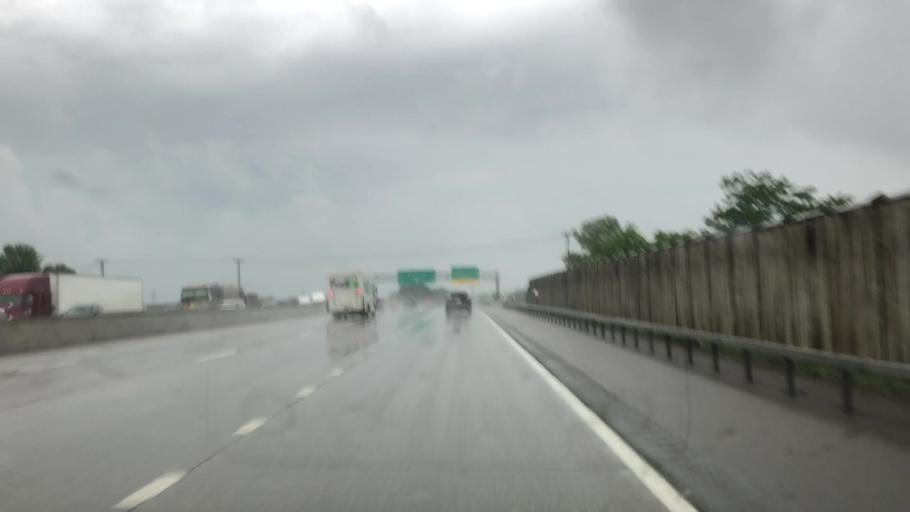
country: US
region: New York
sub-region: Erie County
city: Sloan
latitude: 42.8770
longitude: -78.7834
